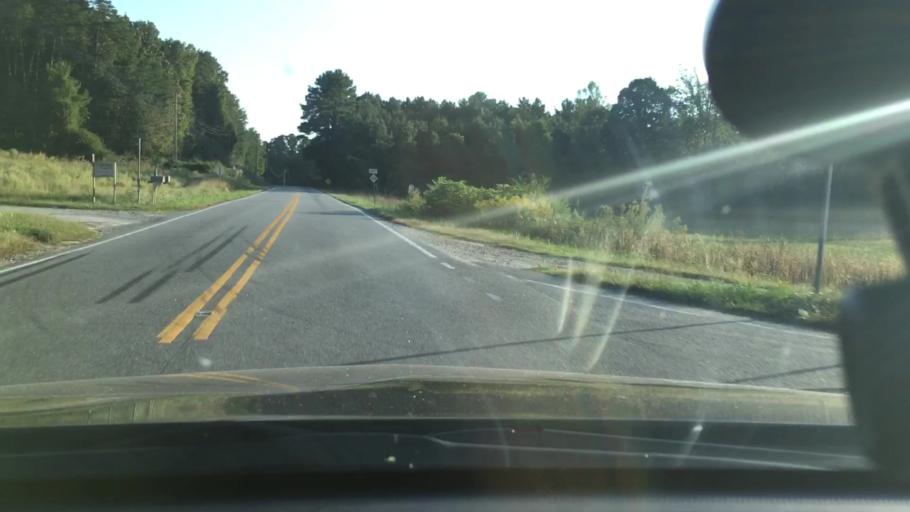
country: US
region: North Carolina
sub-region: Rutherford County
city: Rutherfordton
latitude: 35.3581
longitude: -81.9848
